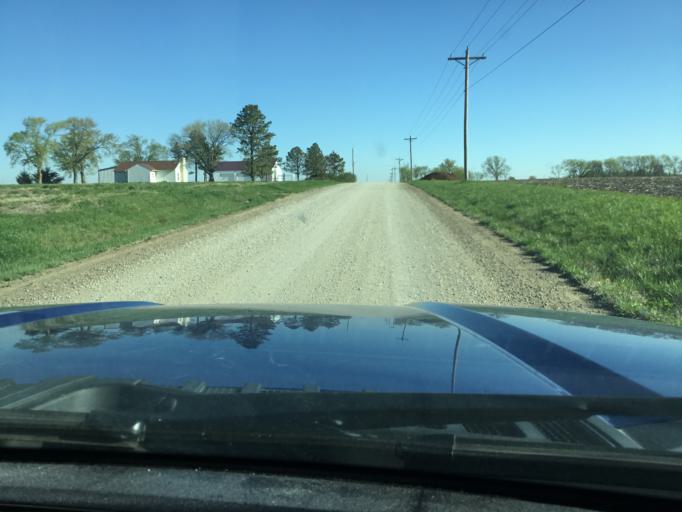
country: US
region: Kansas
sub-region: Douglas County
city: Lawrence
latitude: 38.9648
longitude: -95.3538
